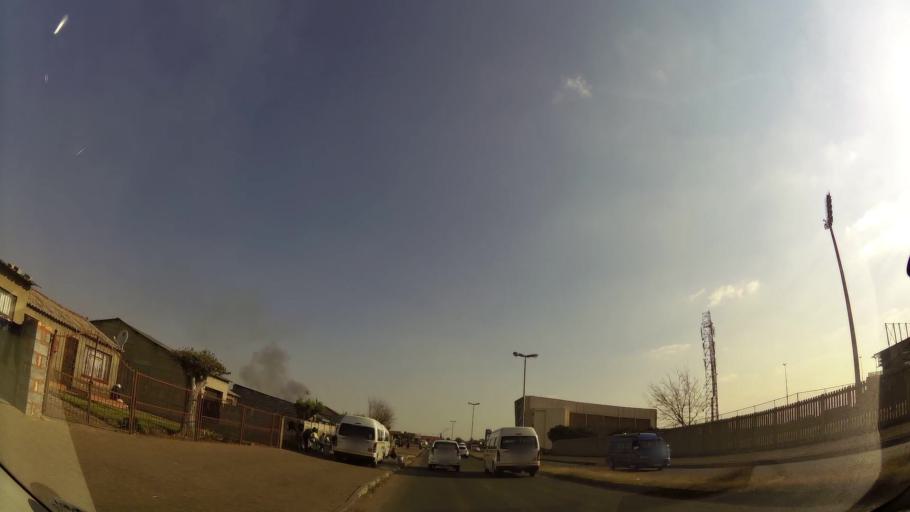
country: ZA
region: Gauteng
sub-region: Ekurhuleni Metropolitan Municipality
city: Brakpan
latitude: -26.1444
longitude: 28.4232
